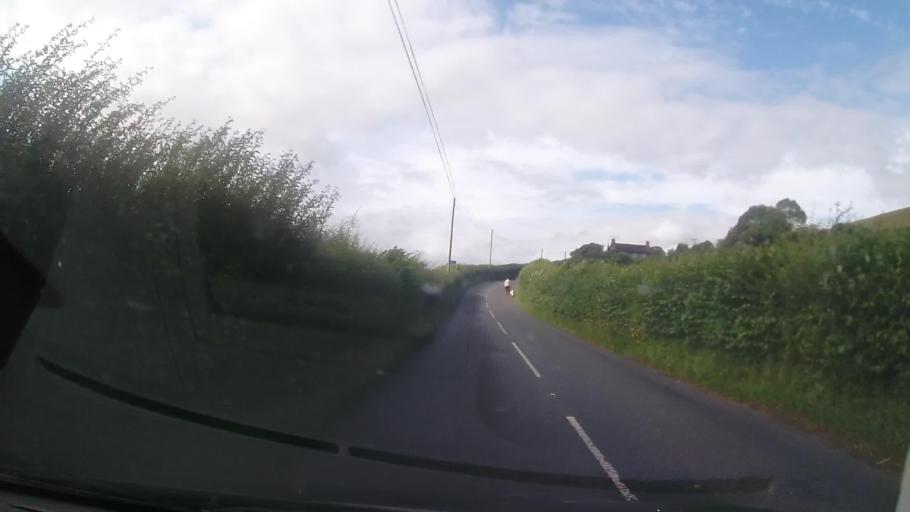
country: GB
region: England
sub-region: Shropshire
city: Acton
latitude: 52.4316
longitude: -3.0350
